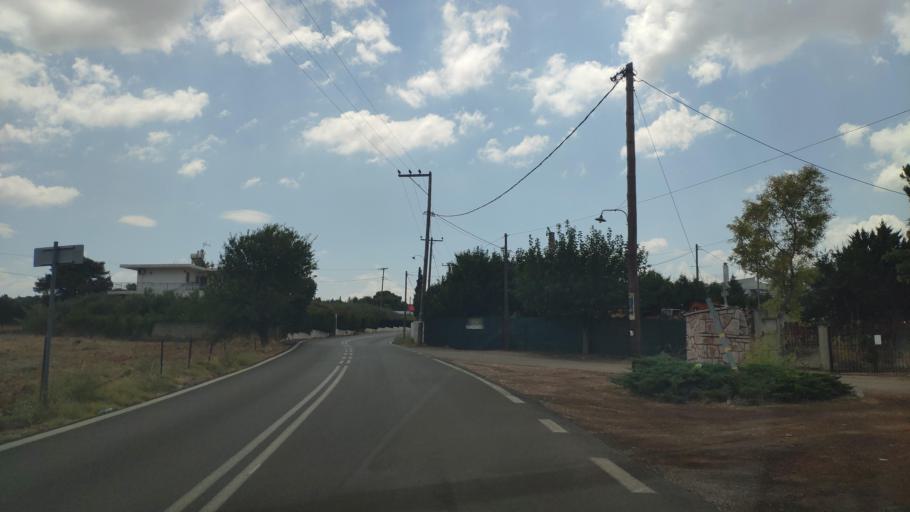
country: GR
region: Central Greece
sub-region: Nomos Fthiotidos
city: Malesina
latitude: 38.6519
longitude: 23.1963
